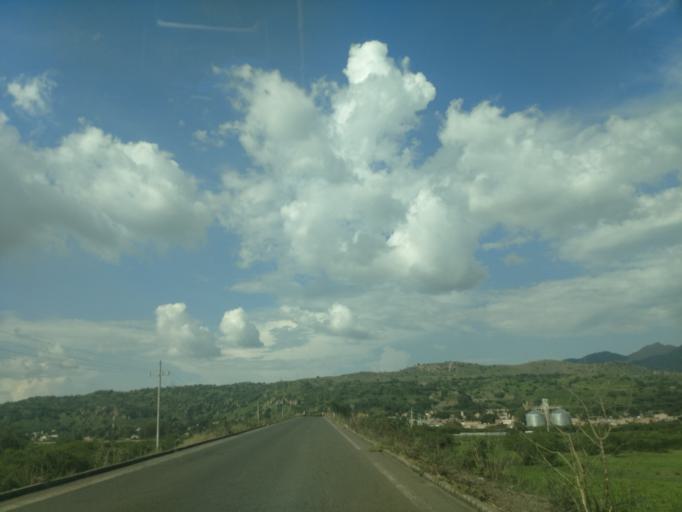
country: MX
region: Jalisco
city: Antonio Escobedo
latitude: 20.9057
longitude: -103.9938
